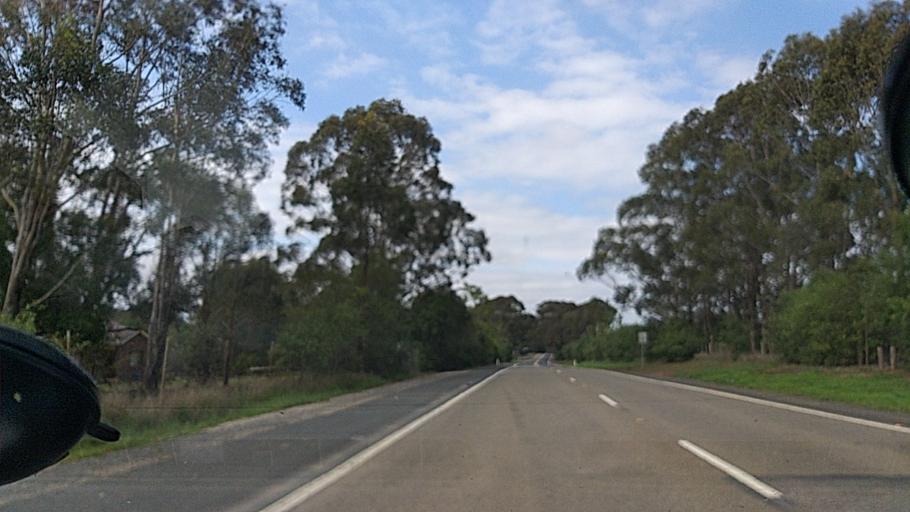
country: AU
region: New South Wales
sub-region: Campbelltown Municipality
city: Glen Alpine
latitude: -34.0830
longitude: 150.7769
